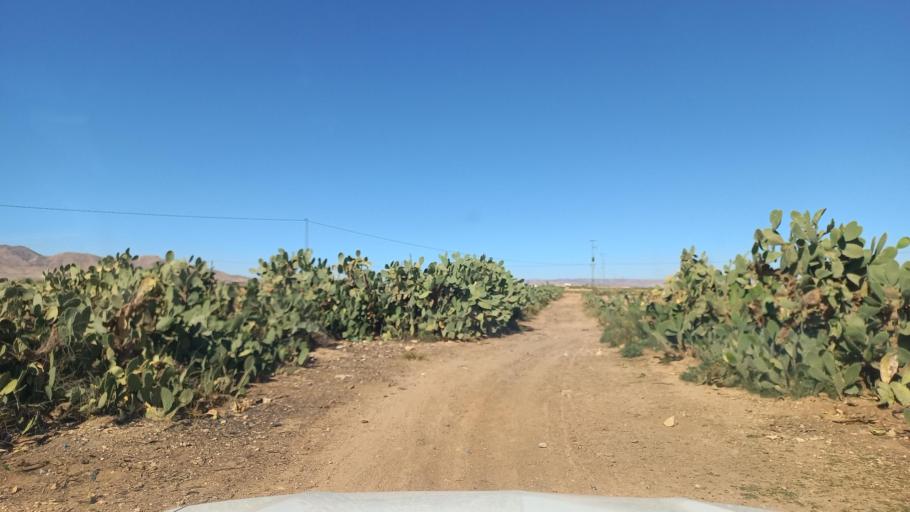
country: TN
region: Al Qasrayn
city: Sbiba
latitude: 35.3831
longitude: 9.0914
